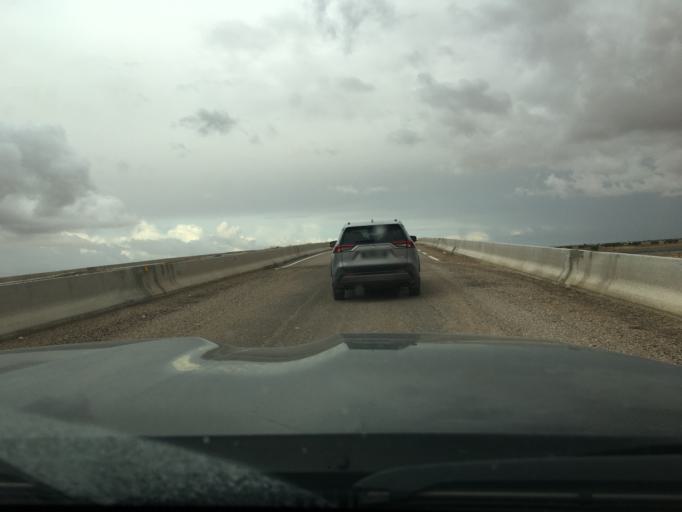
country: TN
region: Madanin
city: Medenine
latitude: 33.2983
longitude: 10.6084
